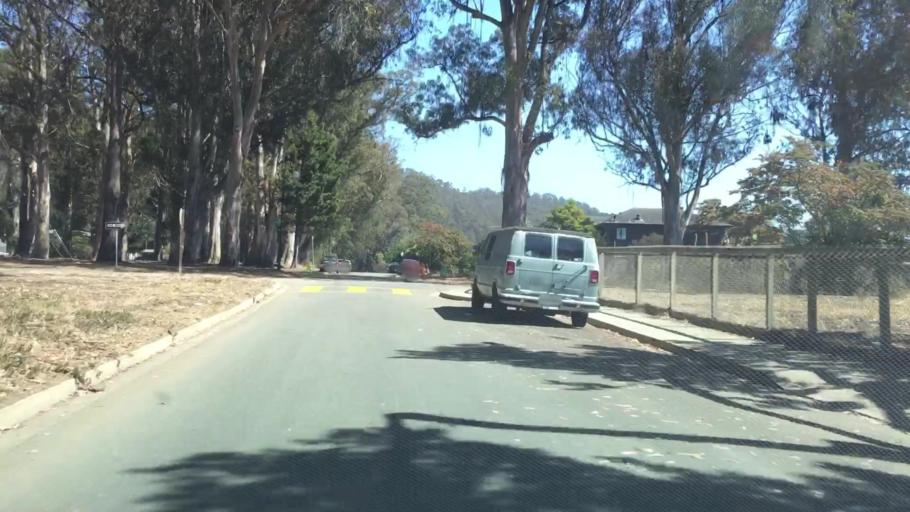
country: US
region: California
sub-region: San Mateo County
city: El Granada
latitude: 37.5014
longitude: -122.4664
